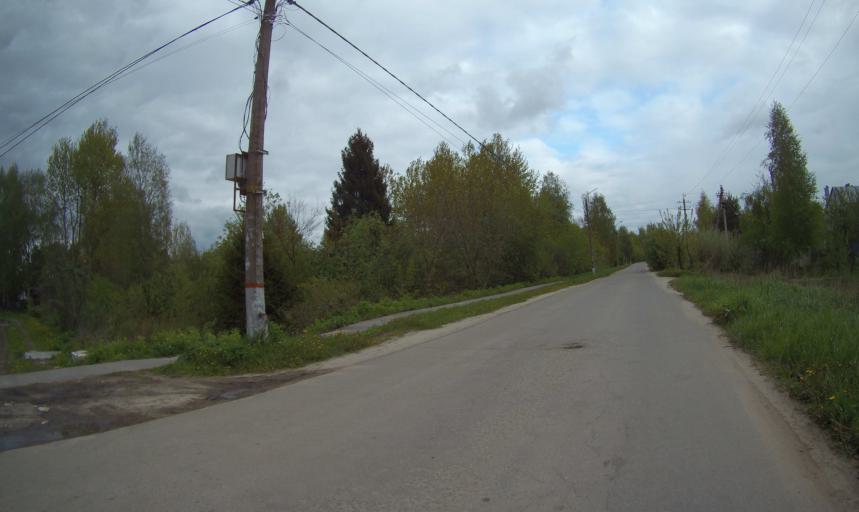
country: RU
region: Moskovskaya
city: Rechitsy
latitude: 55.6087
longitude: 38.5421
